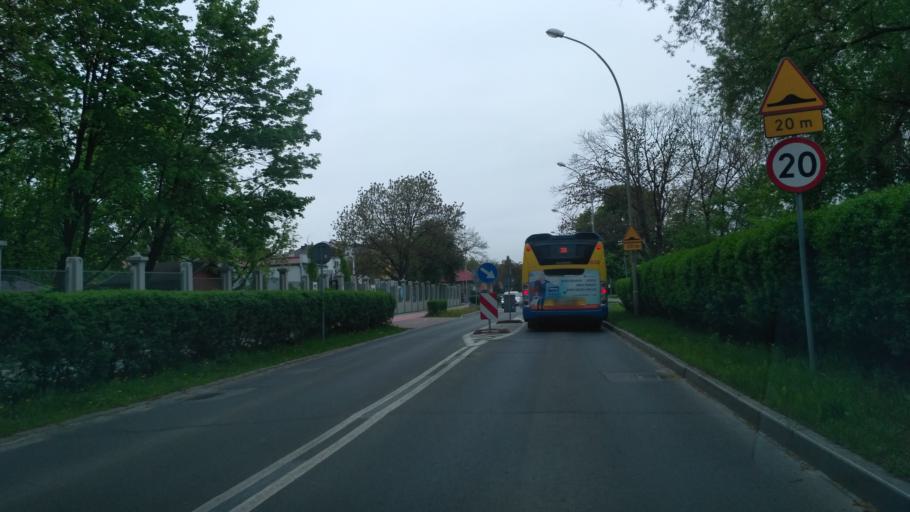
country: PL
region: Lesser Poland Voivodeship
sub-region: Powiat tarnowski
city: Tarnow
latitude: 50.0212
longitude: 20.9856
